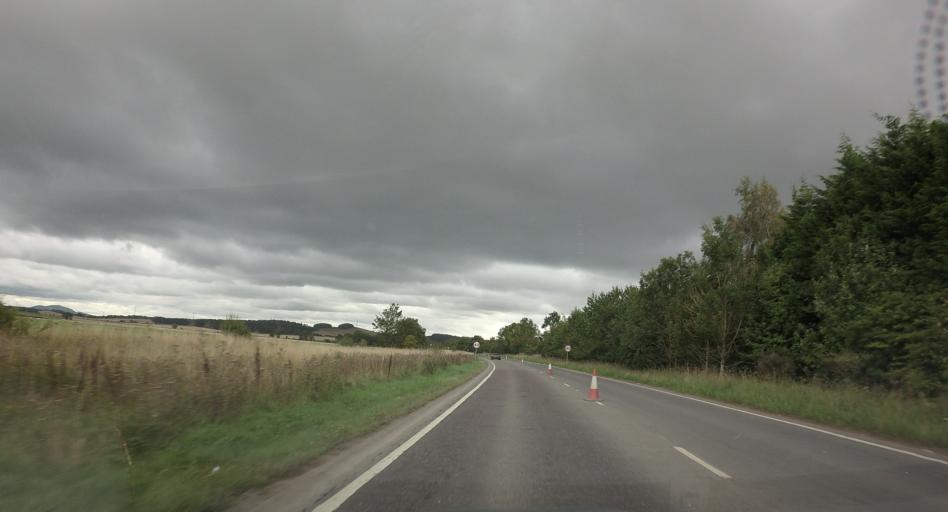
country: GB
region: Scotland
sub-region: Clackmannanshire
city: Clackmannan
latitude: 56.1064
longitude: -3.7387
